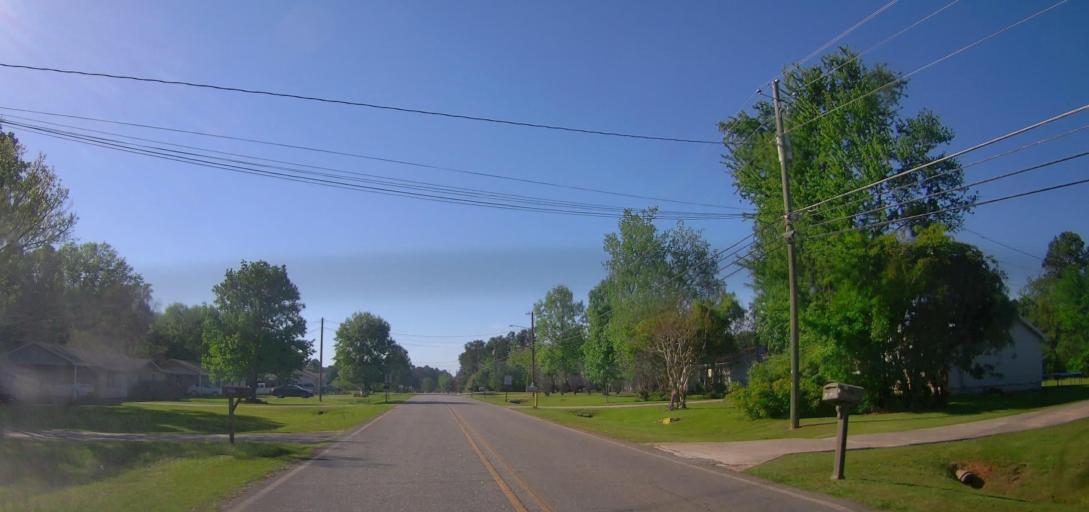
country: US
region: Georgia
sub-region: Houston County
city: Perry
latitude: 32.4684
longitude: -83.7098
